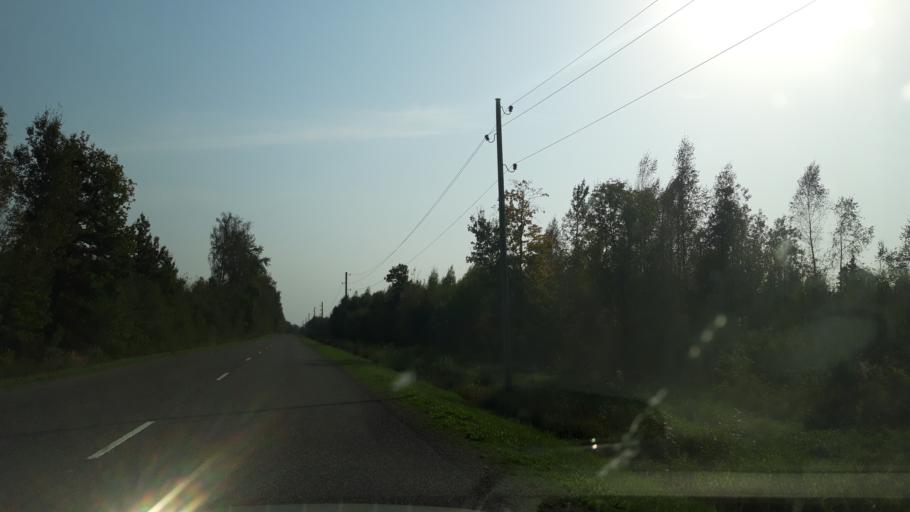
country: LV
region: Burtnieki
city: Matisi
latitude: 57.6351
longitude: 25.2568
